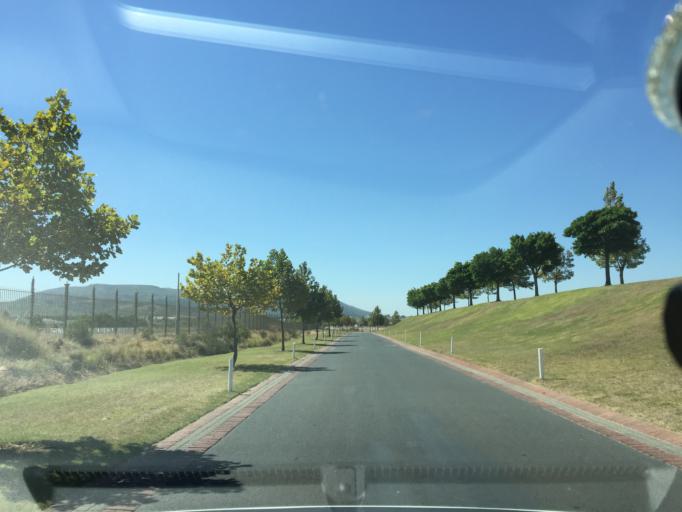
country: ZA
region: Western Cape
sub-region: Cape Winelands District Municipality
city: Paarl
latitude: -33.8072
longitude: 18.9736
